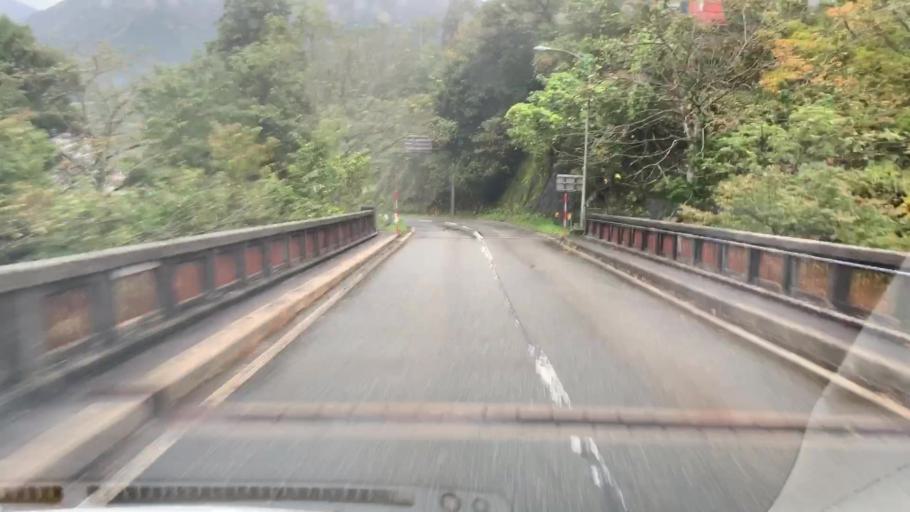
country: JP
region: Toyama
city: Kamiichi
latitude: 36.5739
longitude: 137.3781
